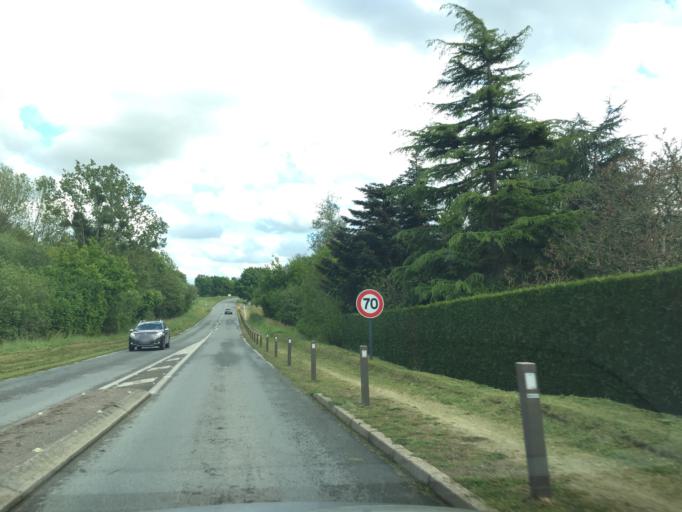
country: FR
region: Brittany
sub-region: Departement des Cotes-d'Armor
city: Ploubalay
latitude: 48.5884
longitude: -2.1453
